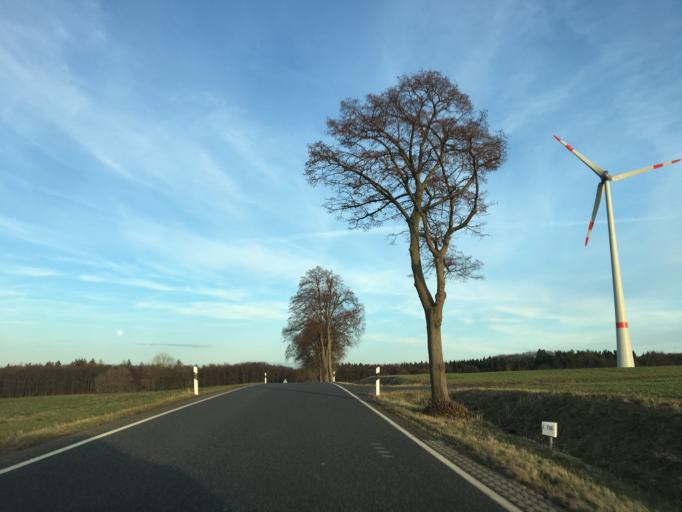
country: DE
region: Hesse
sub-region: Regierungsbezirk Giessen
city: Schwalmtal
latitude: 50.6625
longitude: 9.2865
